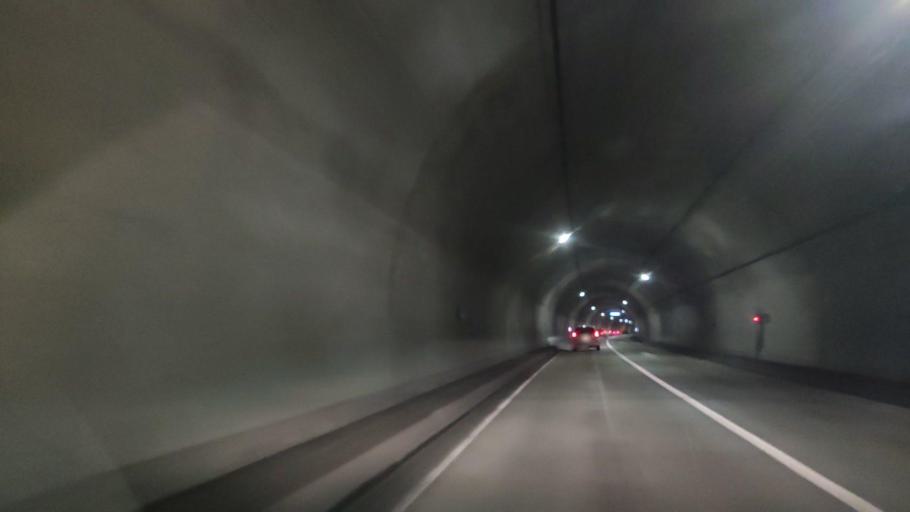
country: JP
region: Hokkaido
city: Ishikari
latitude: 43.5272
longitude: 141.3938
